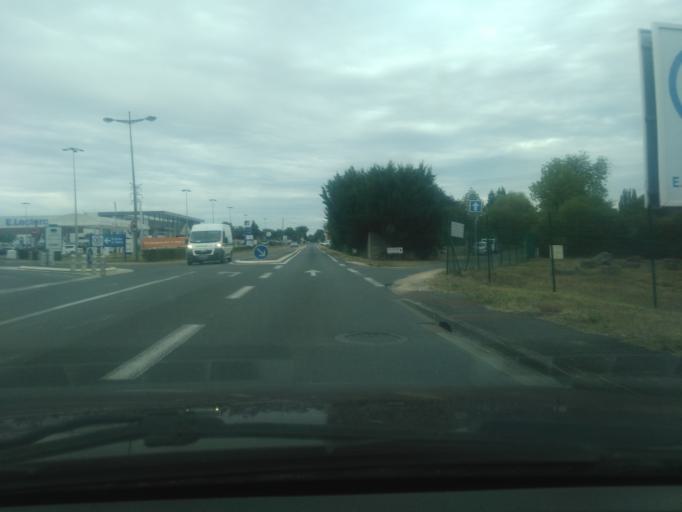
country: FR
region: Centre
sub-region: Departement du Cher
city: Saint-Amand-Montrond
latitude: 46.7217
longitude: 2.5309
